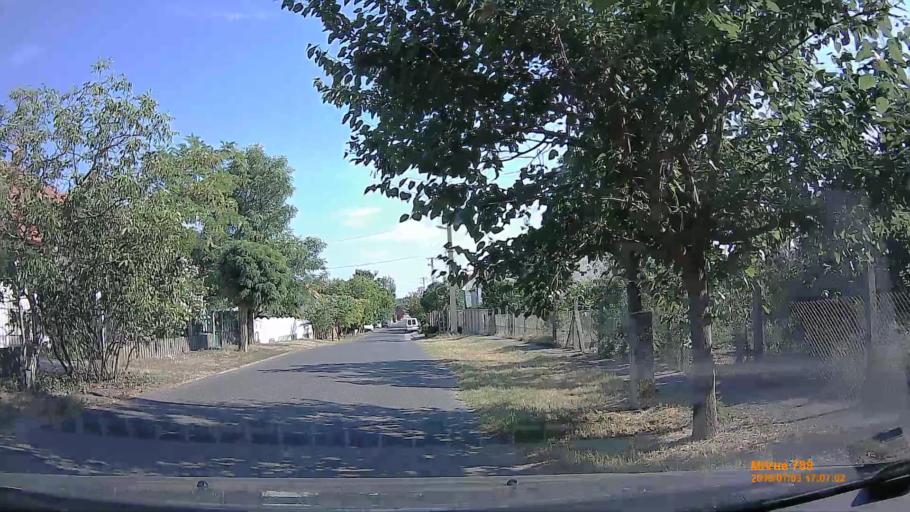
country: HU
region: Gyor-Moson-Sopron
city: Gyor
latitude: 47.7210
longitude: 17.6497
